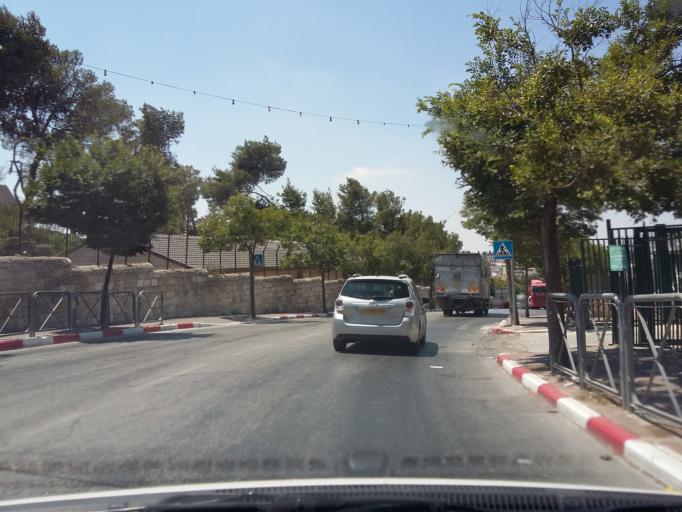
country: PS
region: West Bank
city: East Jerusalem
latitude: 31.7874
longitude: 35.2485
